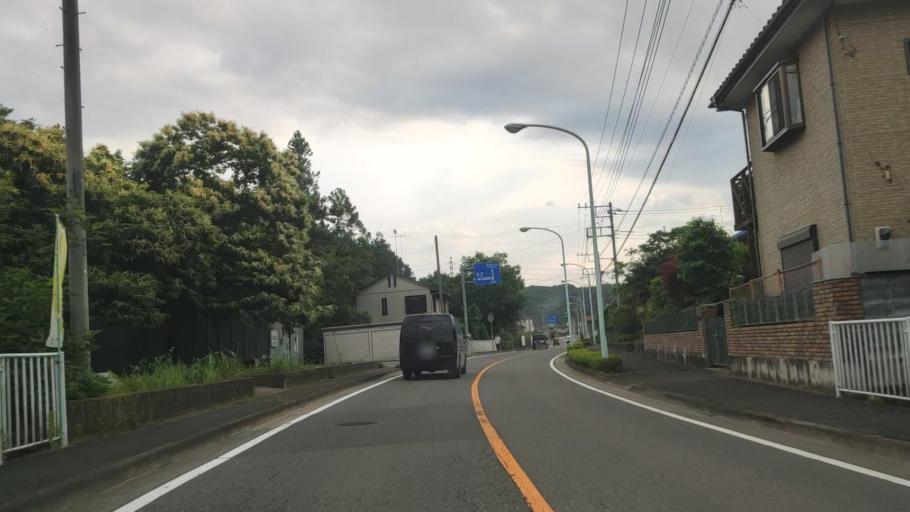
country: JP
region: Saitama
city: Hanno
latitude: 35.8245
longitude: 139.2885
